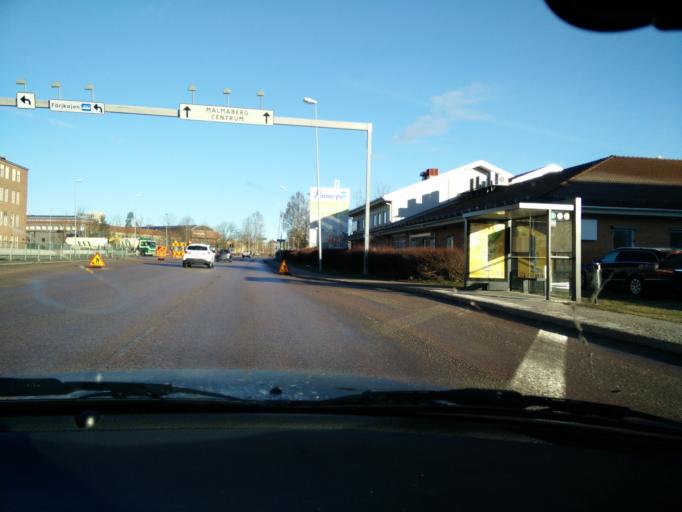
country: SE
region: Vaestmanland
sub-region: Vasteras
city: Vasteras
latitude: 59.6107
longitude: 16.5665
